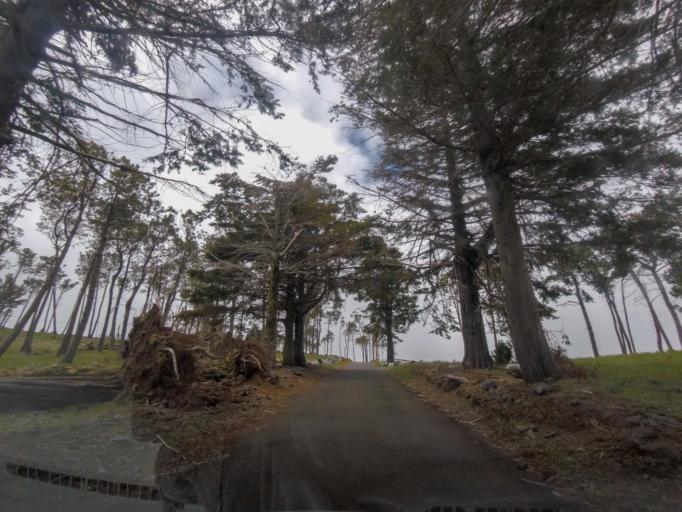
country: PT
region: Madeira
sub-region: Funchal
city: Nossa Senhora do Monte
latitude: 32.7105
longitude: -16.9125
